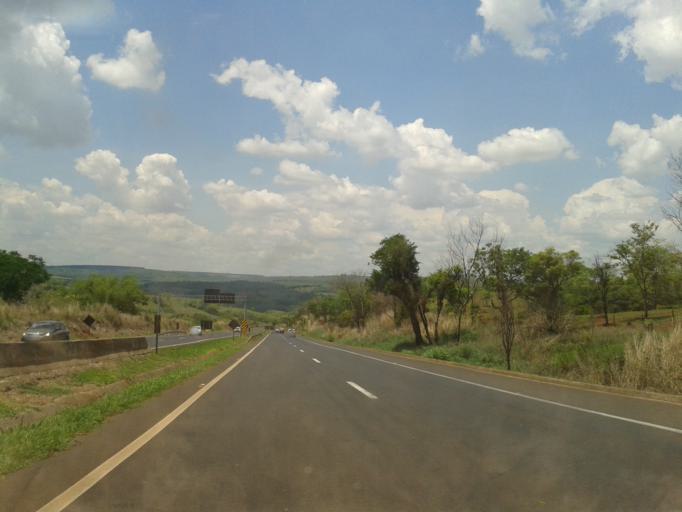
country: BR
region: Minas Gerais
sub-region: Araguari
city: Araguari
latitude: -18.7560
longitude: -48.2406
